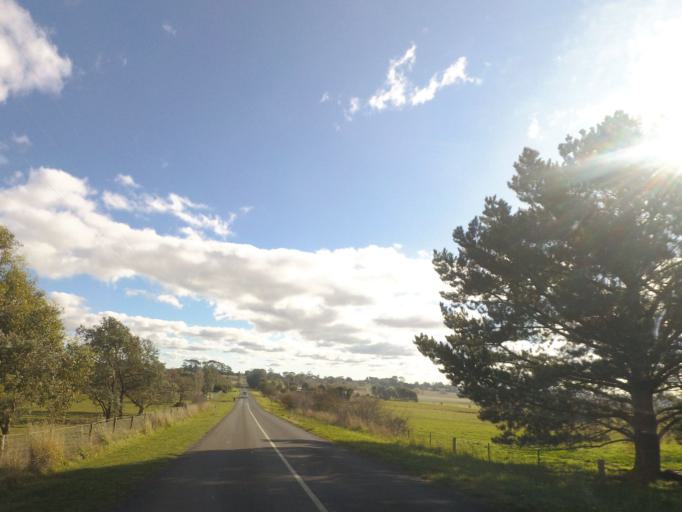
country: AU
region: Victoria
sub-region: Mount Alexander
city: Castlemaine
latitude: -37.2539
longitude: 144.4238
